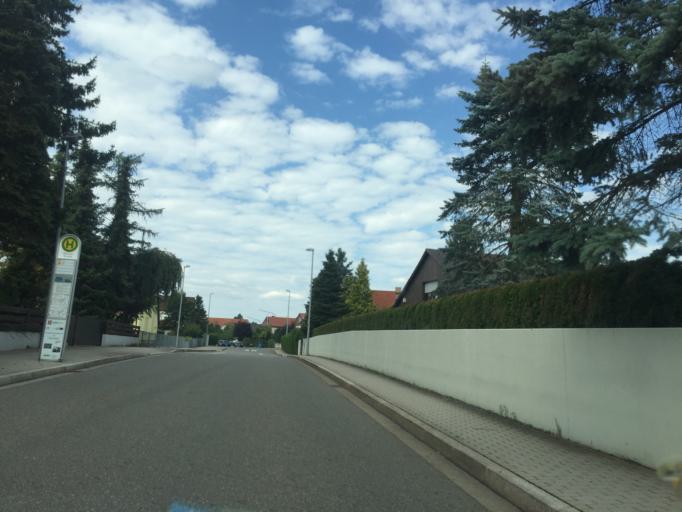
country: DE
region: Bavaria
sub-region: Upper Palatinate
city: Weiden
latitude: 49.6695
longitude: 12.1434
